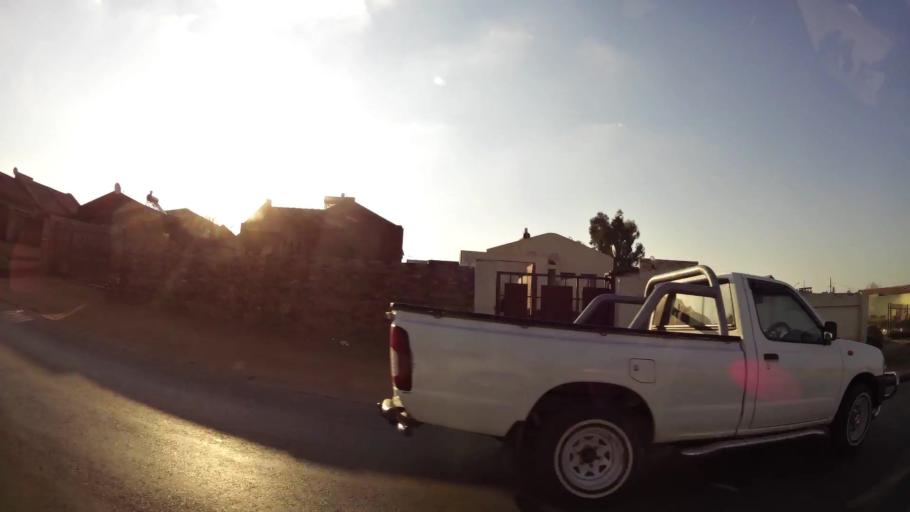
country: ZA
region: Gauteng
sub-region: Ekurhuleni Metropolitan Municipality
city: Tembisa
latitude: -26.0195
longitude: 28.1773
